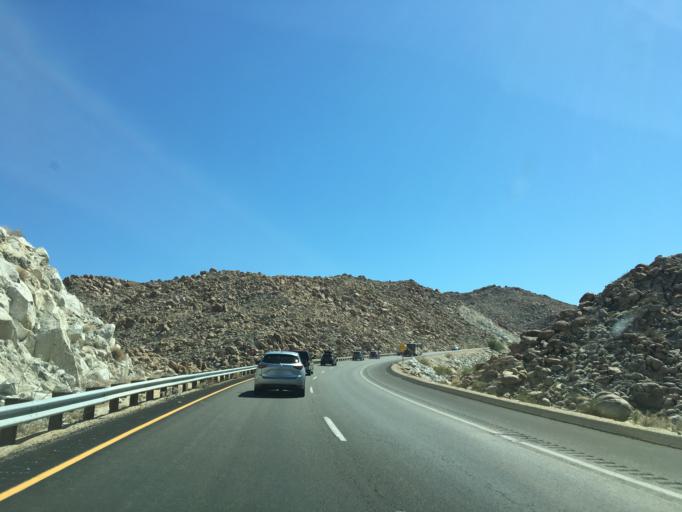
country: MX
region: Baja California
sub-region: Tecate
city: Cereso del Hongo
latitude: 32.7071
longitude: -116.0655
